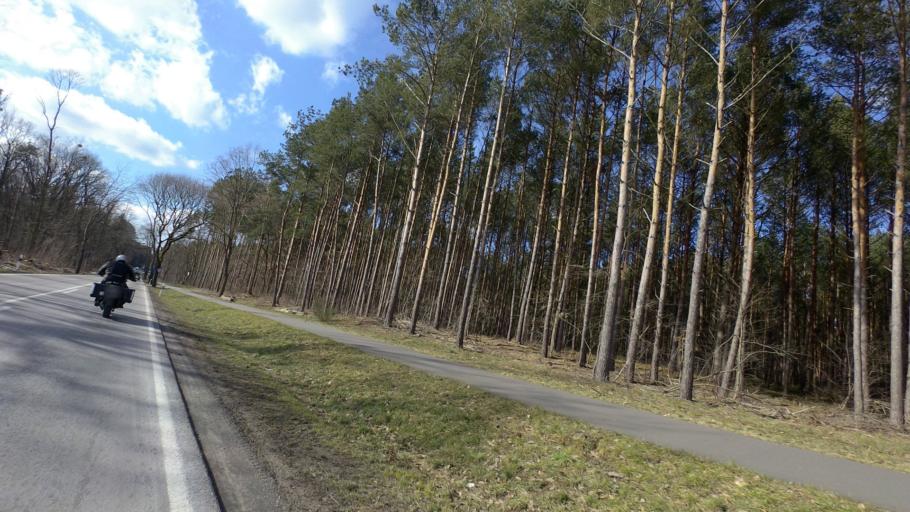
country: DE
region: Brandenburg
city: Marienwerder
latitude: 52.8526
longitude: 13.6645
